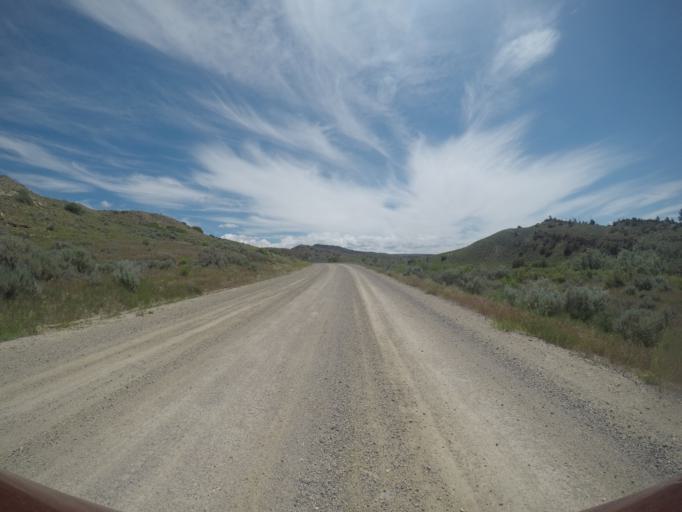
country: US
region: Montana
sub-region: Carbon County
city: Red Lodge
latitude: 45.2095
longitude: -108.8340
